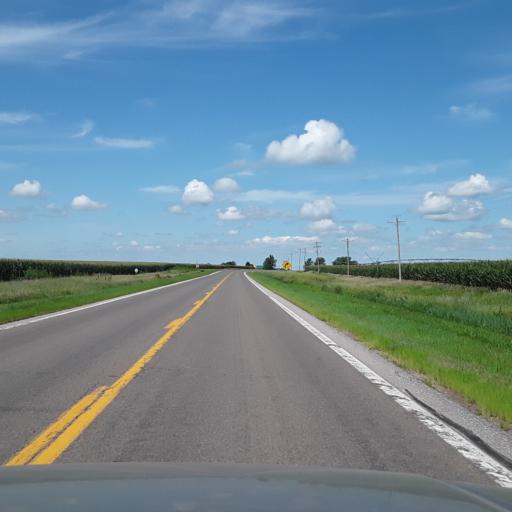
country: US
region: Nebraska
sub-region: Polk County
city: Osceola
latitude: 41.0759
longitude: -97.4178
